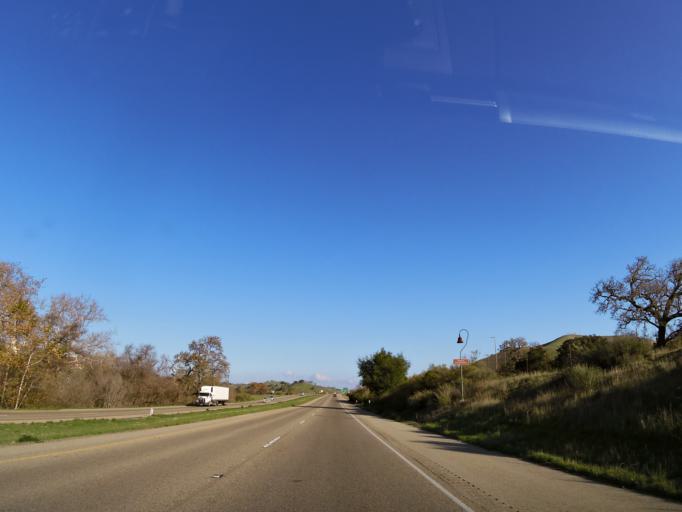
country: US
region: California
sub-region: Santa Barbara County
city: Los Olivos
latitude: 34.6777
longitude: -120.1575
